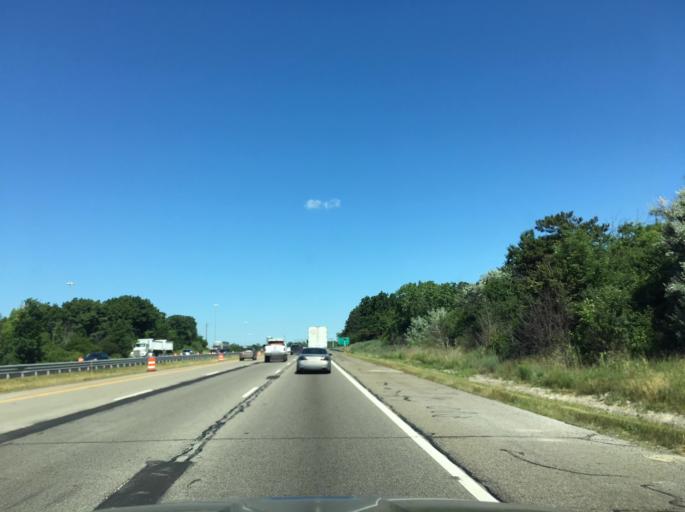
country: US
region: Michigan
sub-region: Oakland County
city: Auburn Hills
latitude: 42.6976
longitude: -83.2756
